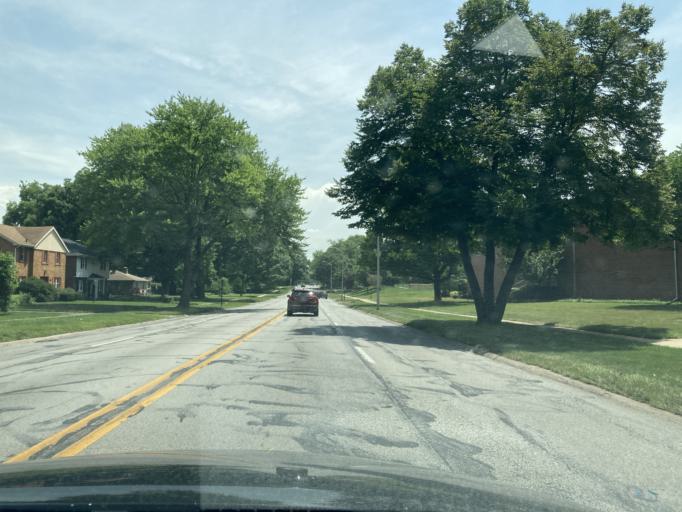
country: US
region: Indiana
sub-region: Marion County
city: Broad Ripple
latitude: 39.8623
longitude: -86.1281
